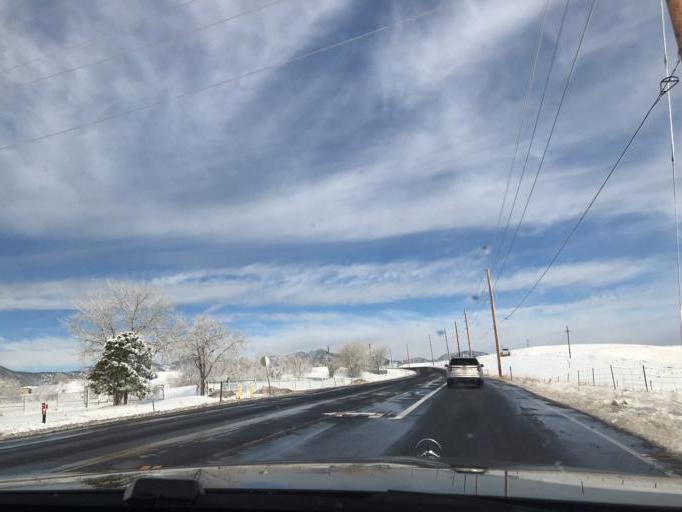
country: US
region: Colorado
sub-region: Boulder County
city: Superior
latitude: 39.8607
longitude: -105.1958
